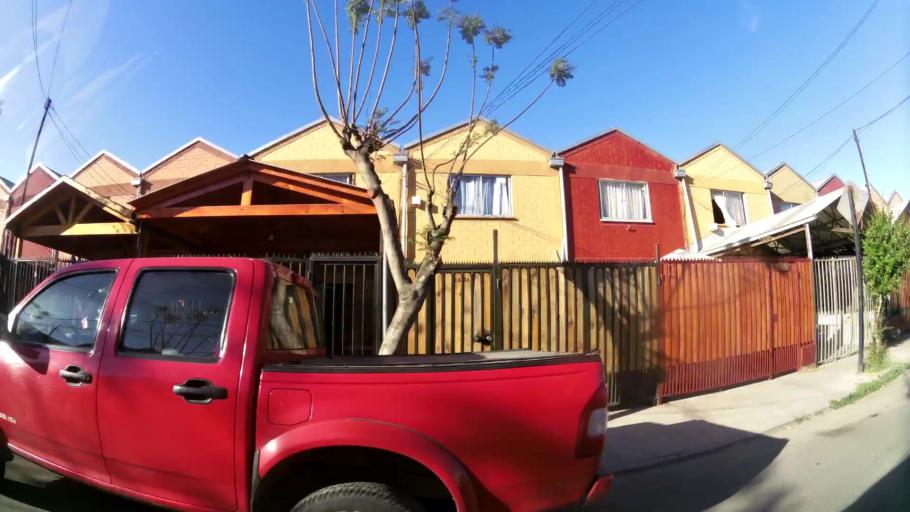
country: CL
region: Santiago Metropolitan
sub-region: Provincia de Maipo
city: San Bernardo
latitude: -33.6013
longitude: -70.6762
